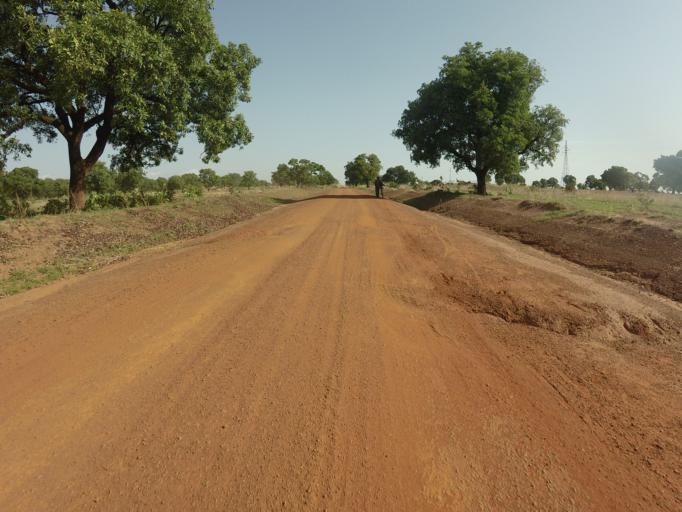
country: GH
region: Upper East
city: Bawku
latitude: 10.7707
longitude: -0.1946
